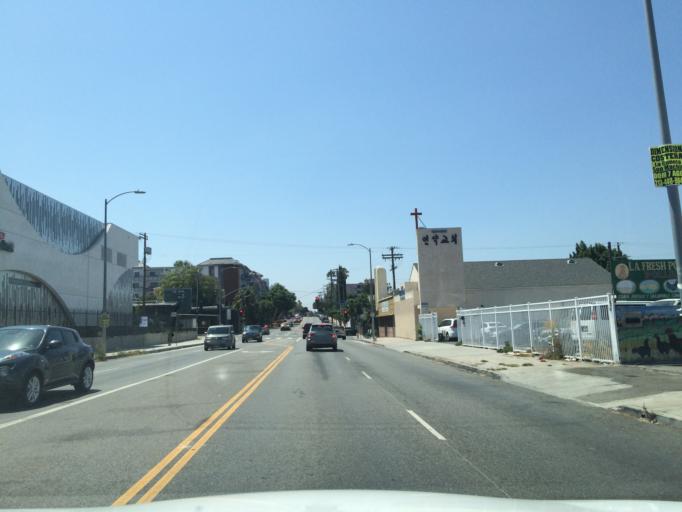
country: US
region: California
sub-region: Los Angeles County
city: Silver Lake
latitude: 34.0744
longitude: -118.2869
